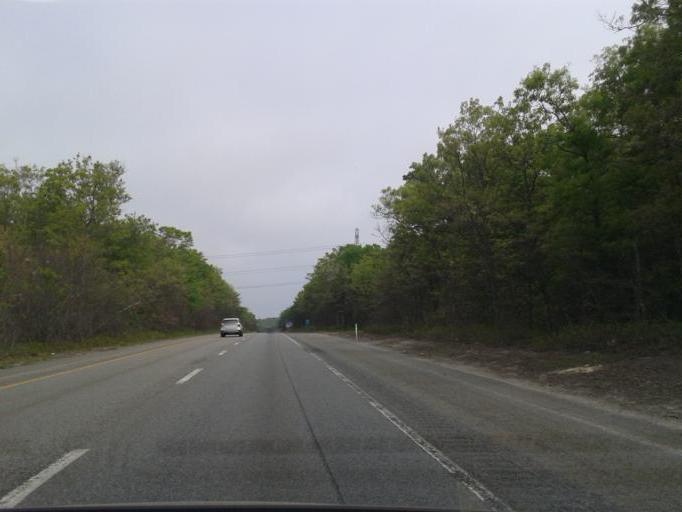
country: US
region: Massachusetts
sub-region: Plymouth County
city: Plymouth
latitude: 41.9058
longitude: -70.6174
